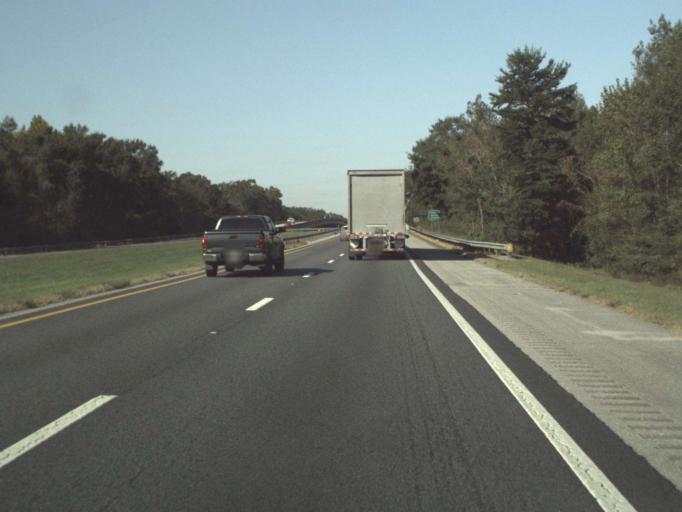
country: US
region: Florida
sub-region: Holmes County
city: Bonifay
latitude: 30.7566
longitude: -85.8244
